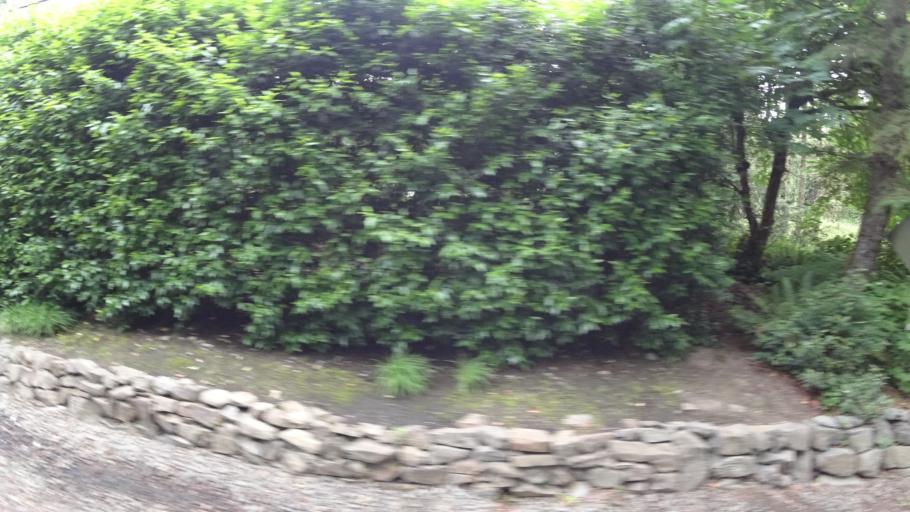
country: US
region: Oregon
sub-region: Clackamas County
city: Lake Oswego
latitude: 45.4340
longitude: -122.6660
